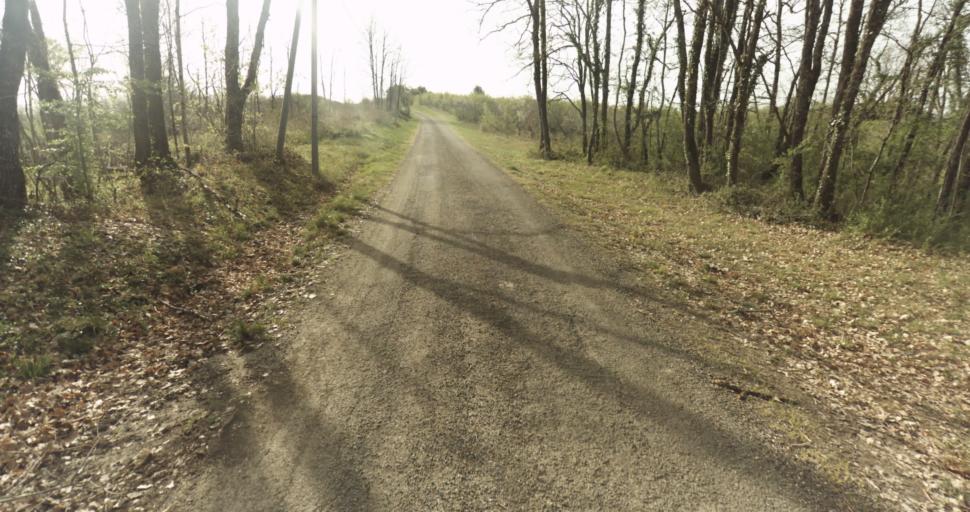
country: FR
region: Midi-Pyrenees
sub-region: Departement du Tarn-et-Garonne
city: Moissac
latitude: 44.1587
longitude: 1.0386
